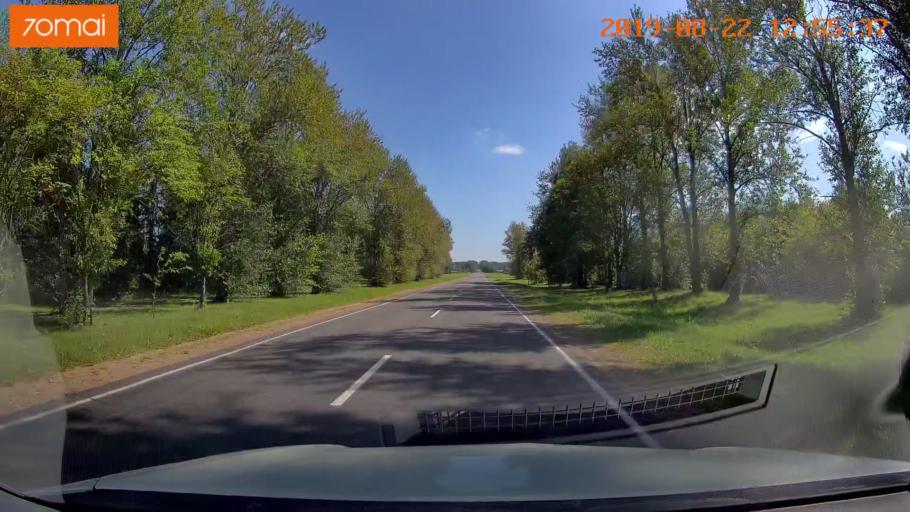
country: BY
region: Minsk
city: Prawdzinski
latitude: 53.4363
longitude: 27.7158
